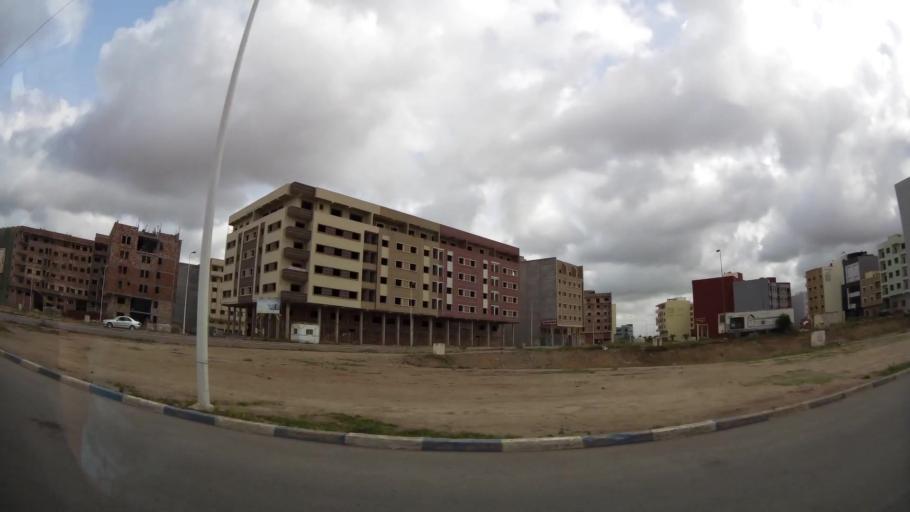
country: MA
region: Oriental
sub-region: Nador
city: Nador
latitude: 35.1529
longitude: -2.9163
